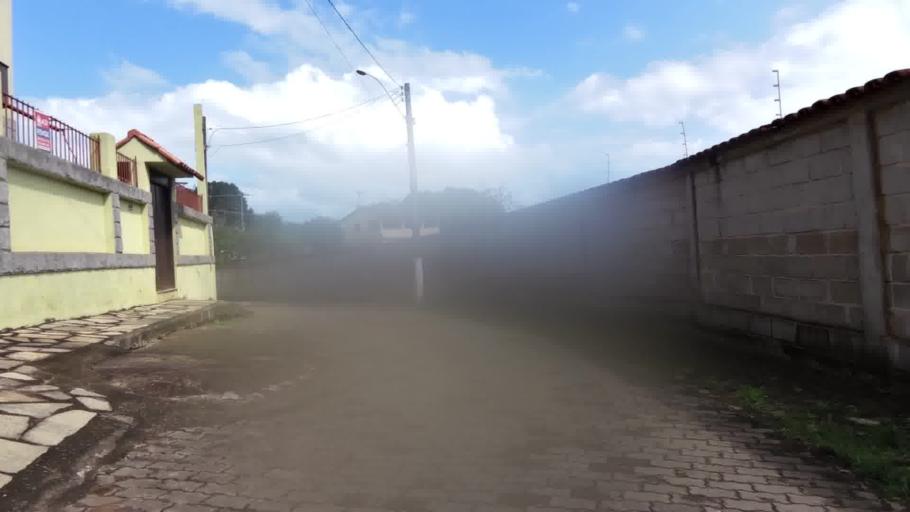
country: BR
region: Espirito Santo
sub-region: Piuma
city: Piuma
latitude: -20.8079
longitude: -40.6575
